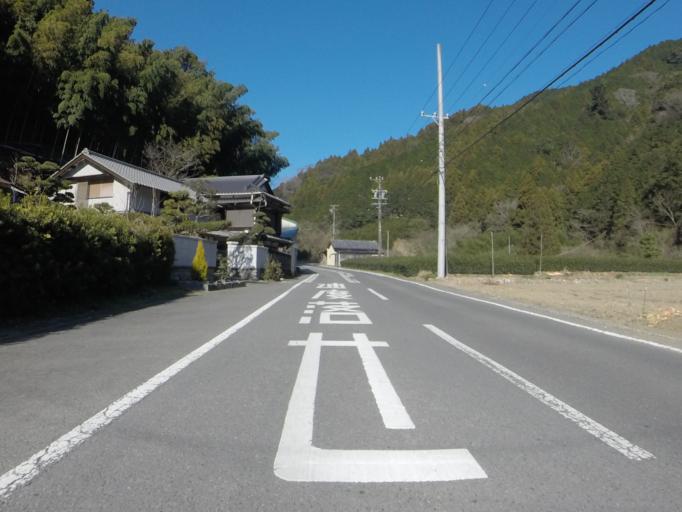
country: JP
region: Shizuoka
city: Fujinomiya
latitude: 35.1292
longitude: 138.4750
